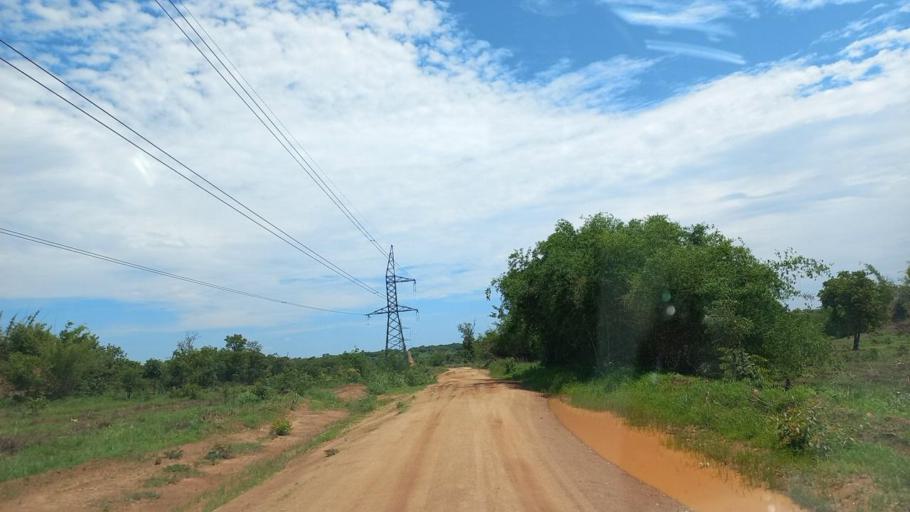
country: ZM
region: Copperbelt
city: Kitwe
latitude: -12.8179
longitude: 28.3551
